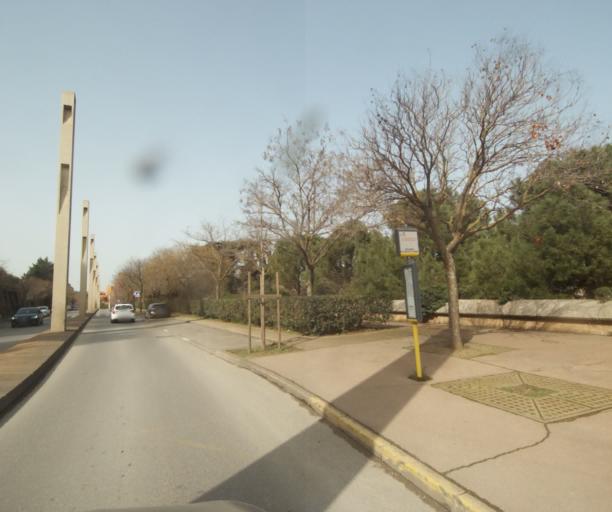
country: FR
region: Provence-Alpes-Cote d'Azur
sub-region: Departement des Bouches-du-Rhone
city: Gardanne
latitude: 43.4525
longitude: 5.4679
